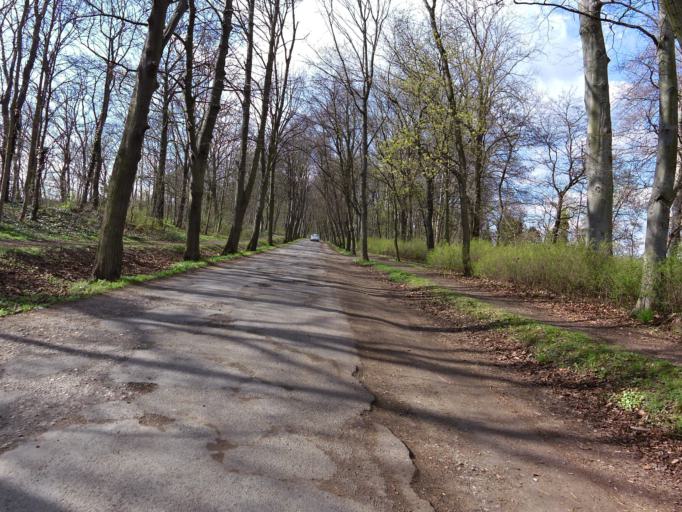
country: DE
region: Thuringia
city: Gotha
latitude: 50.9544
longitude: 10.6862
